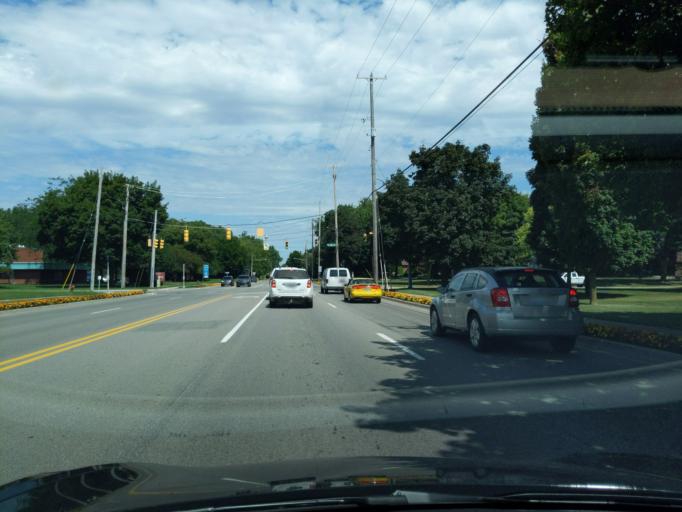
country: US
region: Michigan
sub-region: Midland County
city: Midland
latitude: 43.6246
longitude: -84.2470
